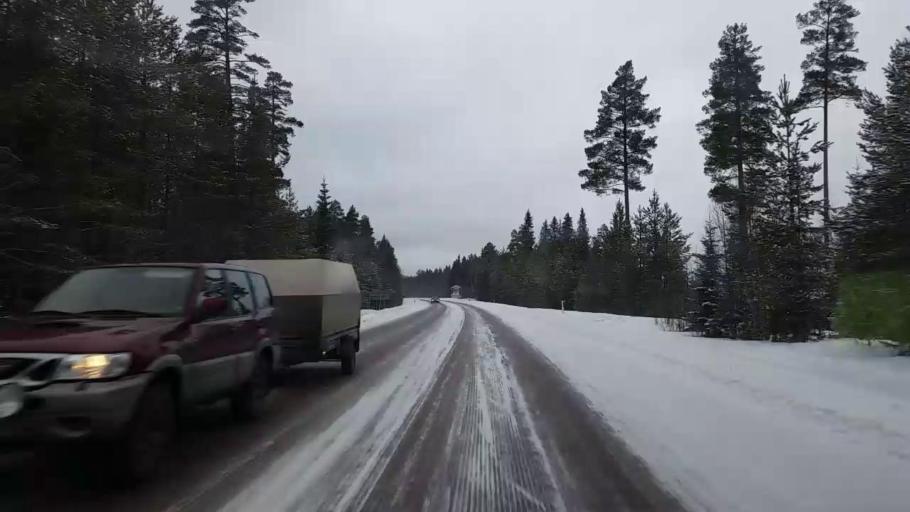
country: SE
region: Jaemtland
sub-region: Bergs Kommun
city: Hoverberg
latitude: 62.4555
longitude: 14.5495
